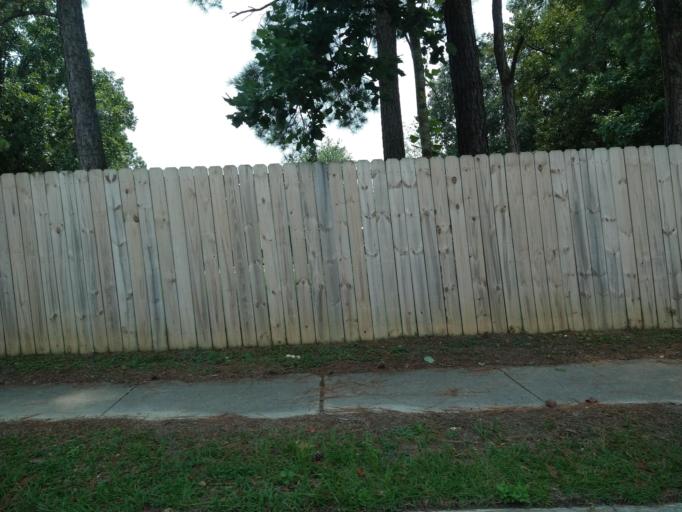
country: US
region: North Carolina
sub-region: Onslow County
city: Pumpkin Center
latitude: 34.7603
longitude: -77.3719
